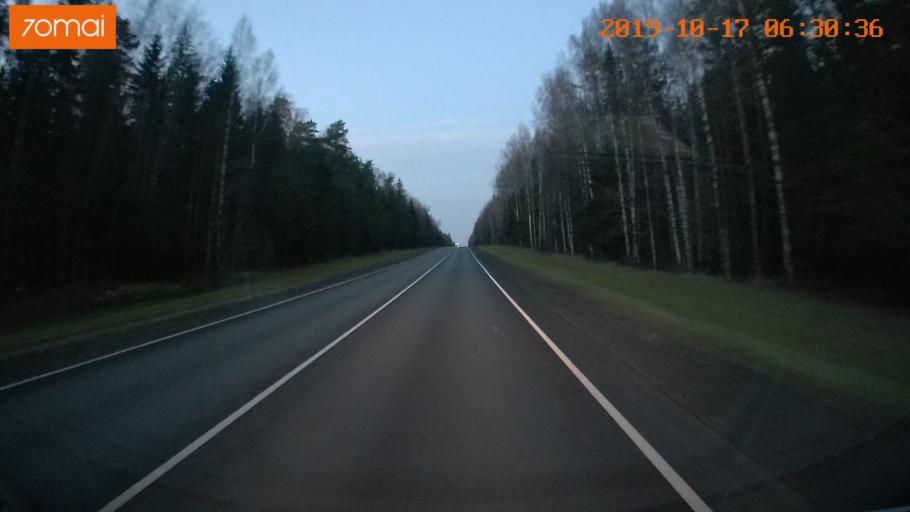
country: RU
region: Ivanovo
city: Lezhnevo
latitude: 56.7348
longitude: 40.7163
